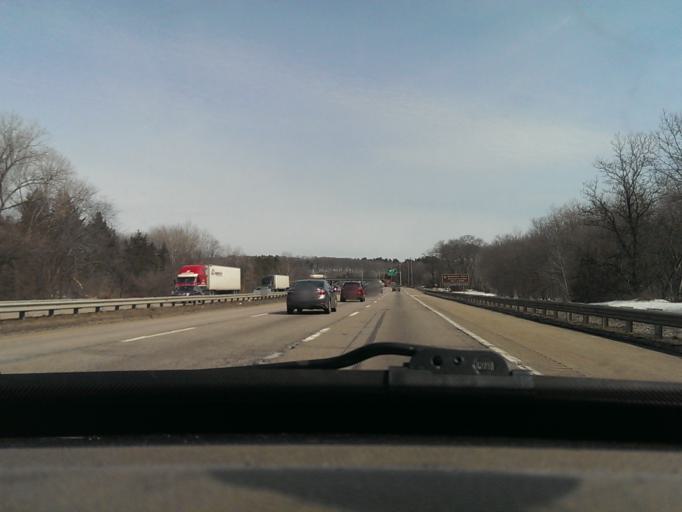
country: US
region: Massachusetts
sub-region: Worcester County
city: Millbury
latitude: 42.2061
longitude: -71.7958
